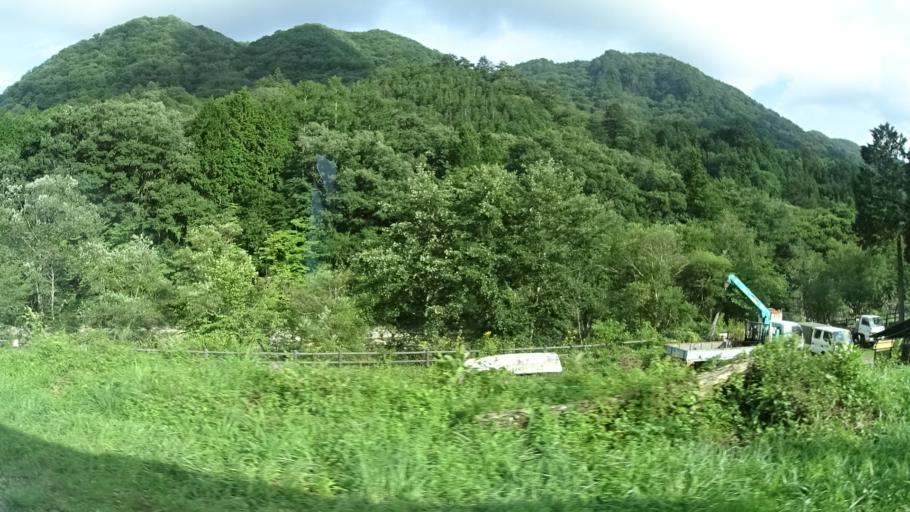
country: JP
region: Tochigi
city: Nikko
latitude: 36.6847
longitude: 139.4931
